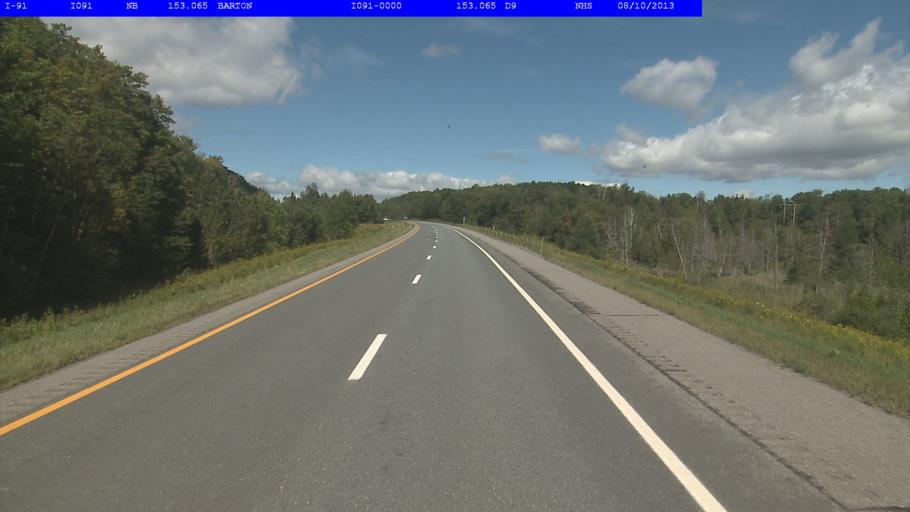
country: US
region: Vermont
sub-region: Caledonia County
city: Lyndonville
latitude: 44.7051
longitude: -72.1508
